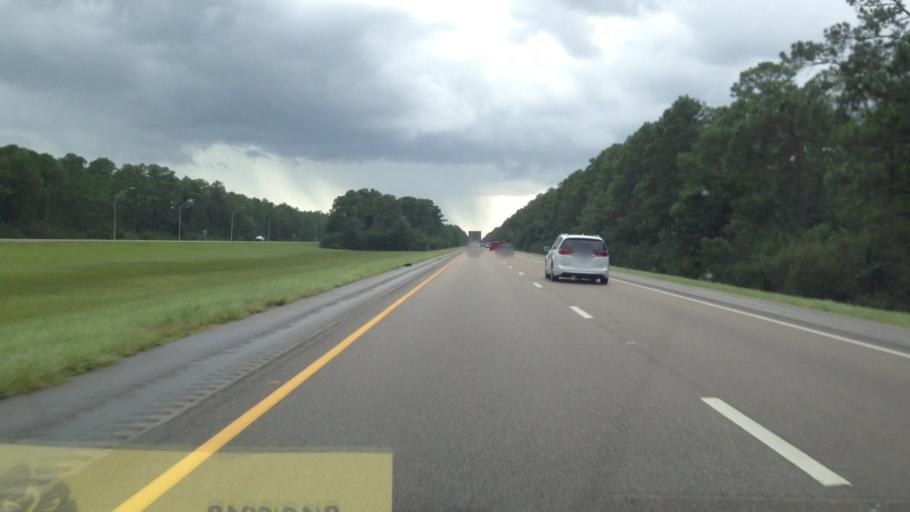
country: US
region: Mississippi
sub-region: Hancock County
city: Kiln
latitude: 30.3480
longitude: -89.4581
